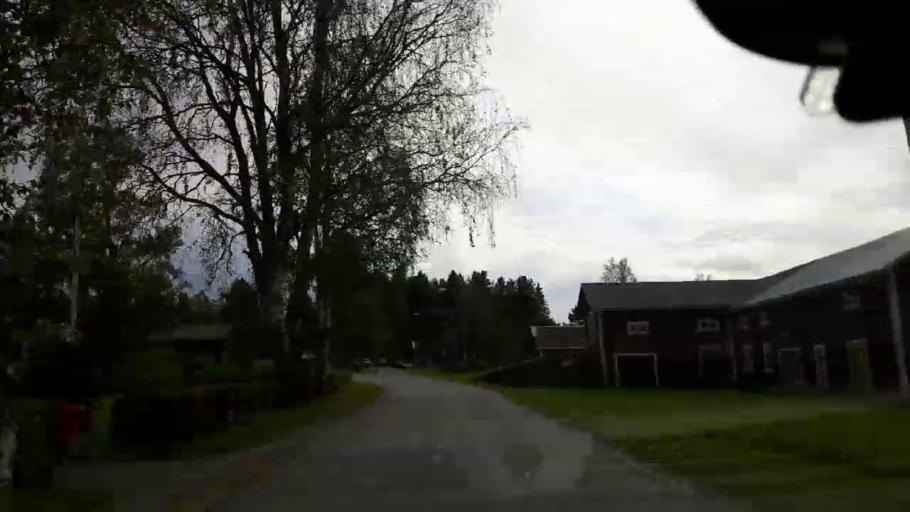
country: SE
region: Jaemtland
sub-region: Ragunda Kommun
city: Hammarstrand
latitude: 63.0077
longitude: 16.0863
